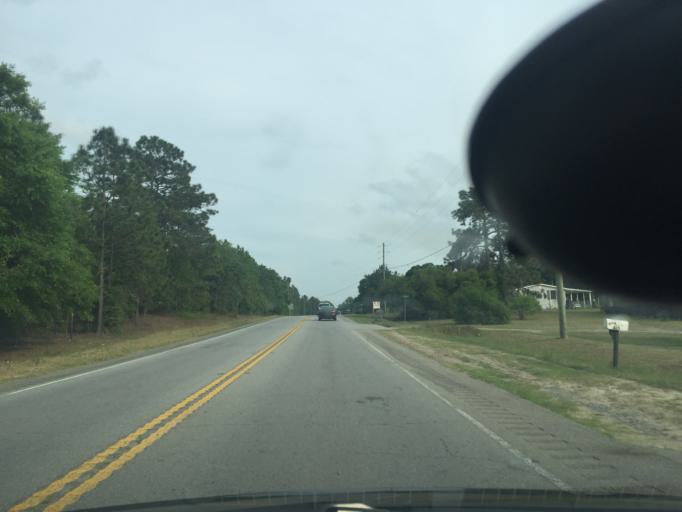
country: US
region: Georgia
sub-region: Bryan County
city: Richmond Hill
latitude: 32.0296
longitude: -81.3220
